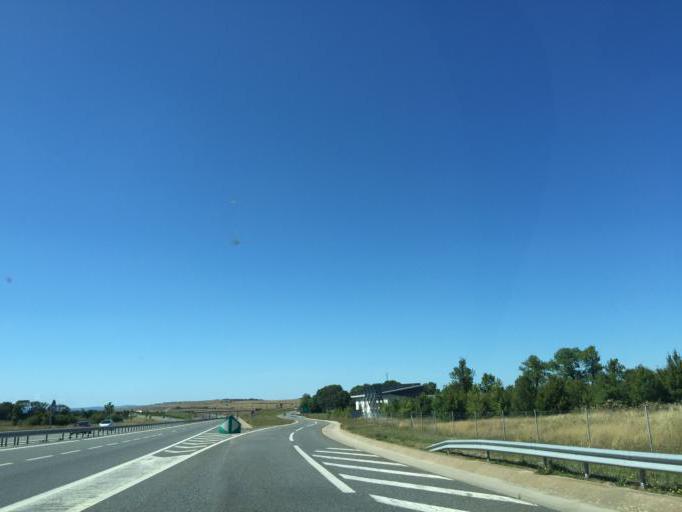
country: FR
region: Midi-Pyrenees
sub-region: Departement de l'Aveyron
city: La Cavalerie
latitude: 44.0079
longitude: 3.1460
